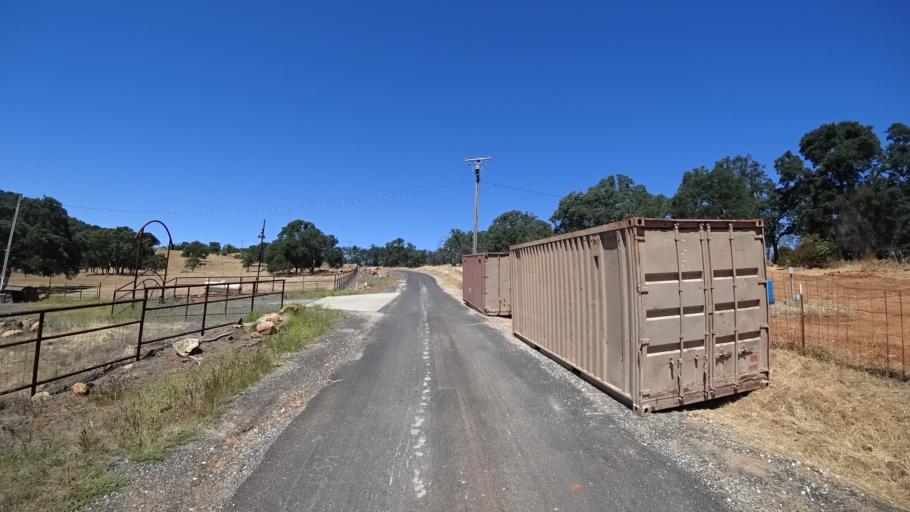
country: US
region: California
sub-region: Calaveras County
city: Copperopolis
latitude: 37.9483
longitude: -120.6925
